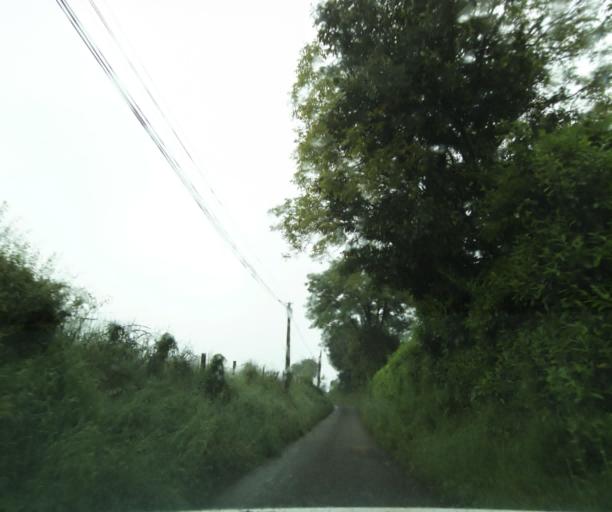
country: FR
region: Bourgogne
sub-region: Departement de Saone-et-Loire
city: Charolles
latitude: 46.4146
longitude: 4.3860
